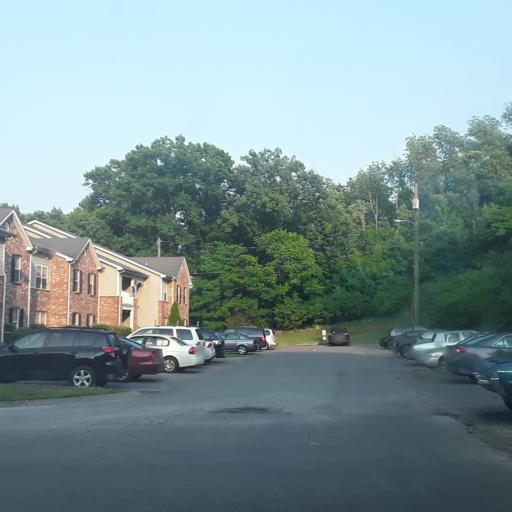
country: US
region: Tennessee
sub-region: Williamson County
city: Brentwood Estates
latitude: 36.0394
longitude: -86.7191
